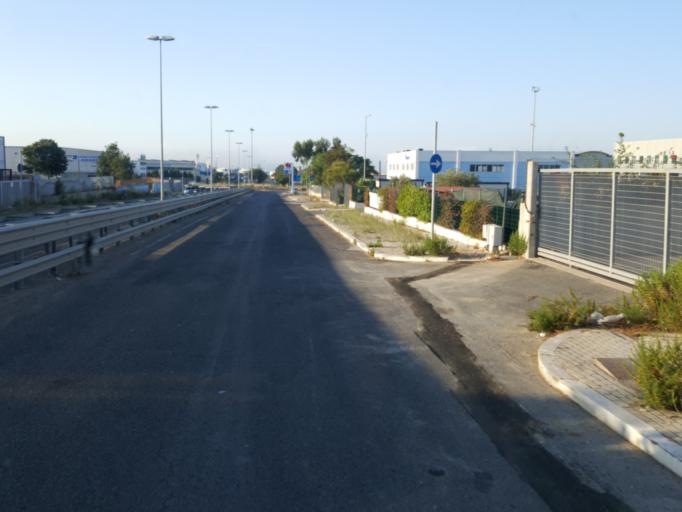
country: IT
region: Latium
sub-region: Citta metropolitana di Roma Capitale
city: Aurelia
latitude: 42.1224
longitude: 11.7781
